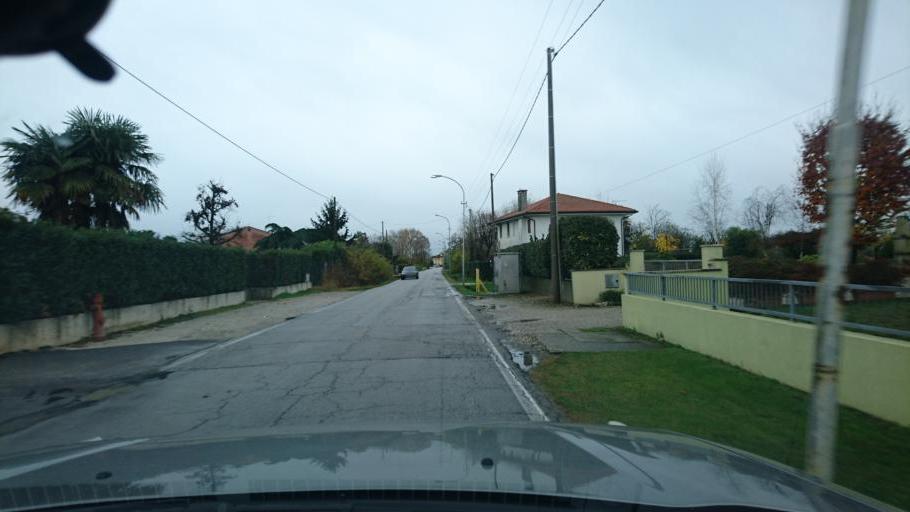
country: IT
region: Veneto
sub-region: Provincia di Treviso
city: Castelfranco Veneto
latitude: 45.6600
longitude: 11.9512
